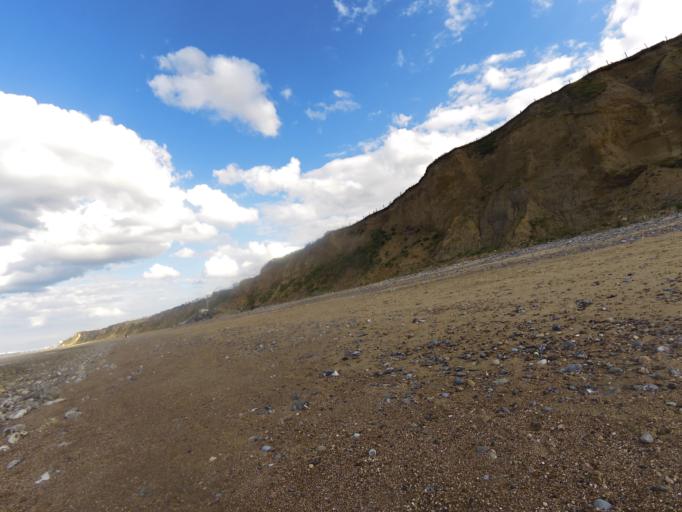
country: GB
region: England
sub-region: Norfolk
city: Cromer
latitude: 52.9381
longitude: 1.2725
